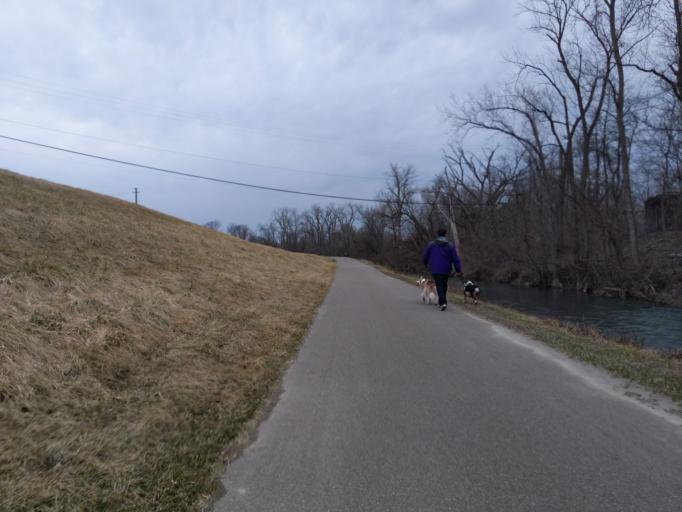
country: US
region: New York
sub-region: Chemung County
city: Elmira
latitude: 42.0961
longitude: -76.7885
